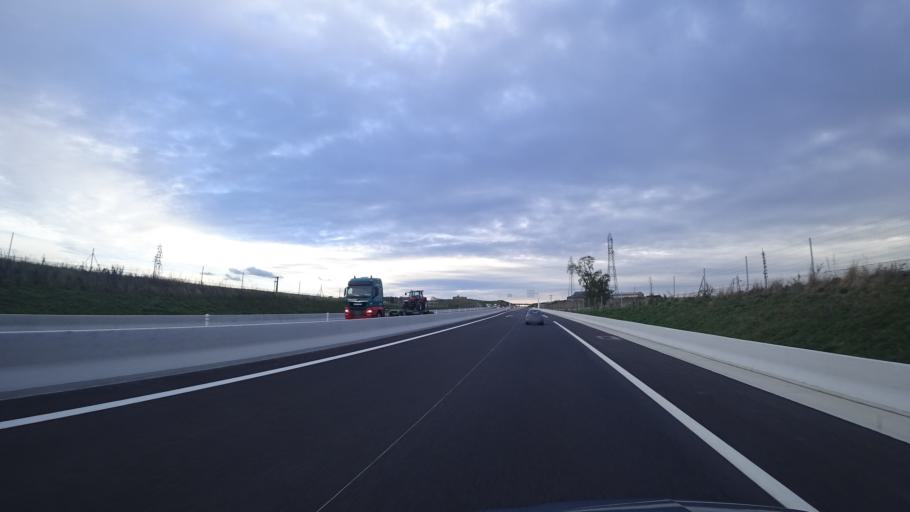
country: FR
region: Midi-Pyrenees
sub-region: Departement de l'Aveyron
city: Baraqueville
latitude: 44.2881
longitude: 2.4313
